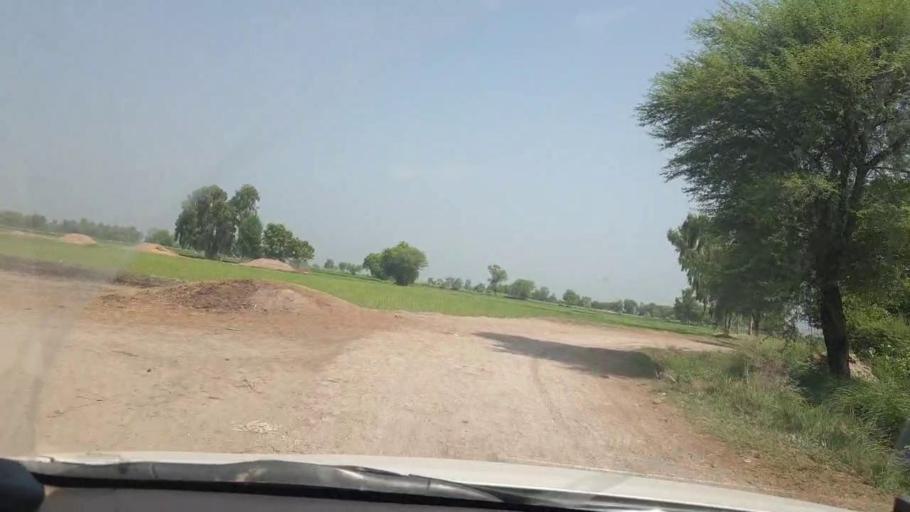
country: PK
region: Sindh
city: Chak
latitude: 27.8832
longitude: 68.7829
